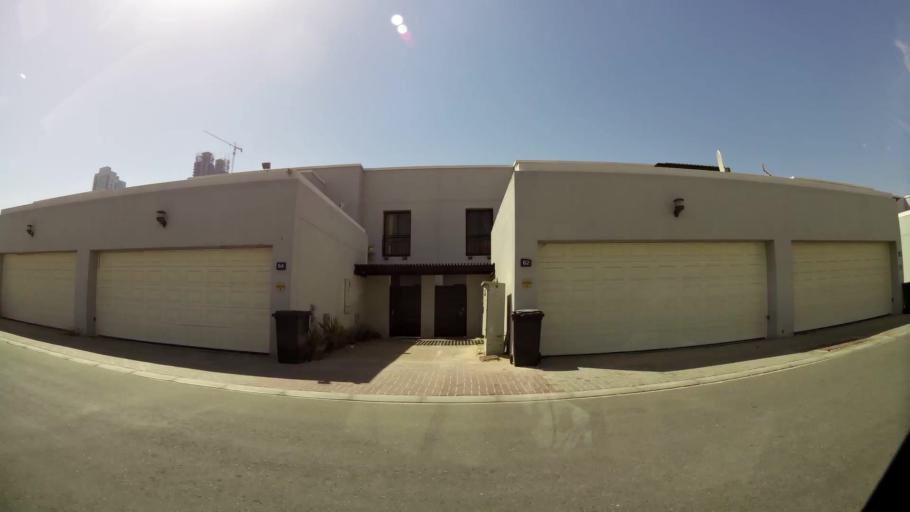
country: AE
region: Dubai
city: Dubai
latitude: 25.1074
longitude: 55.1858
